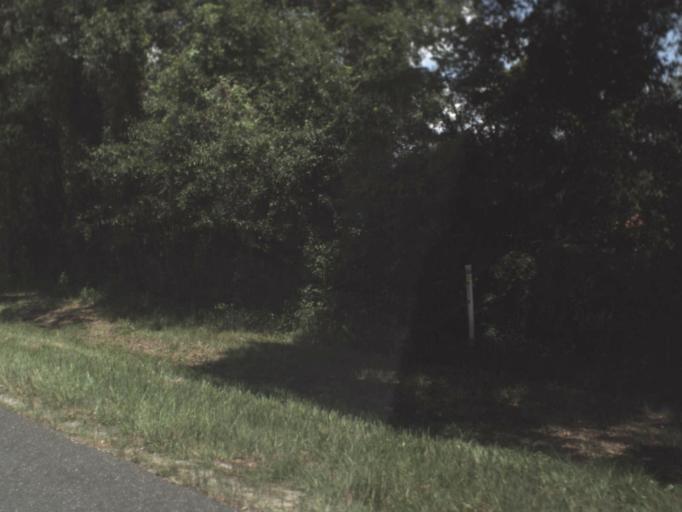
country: US
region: Florida
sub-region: Columbia County
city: Lake City
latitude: 30.1327
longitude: -82.7137
